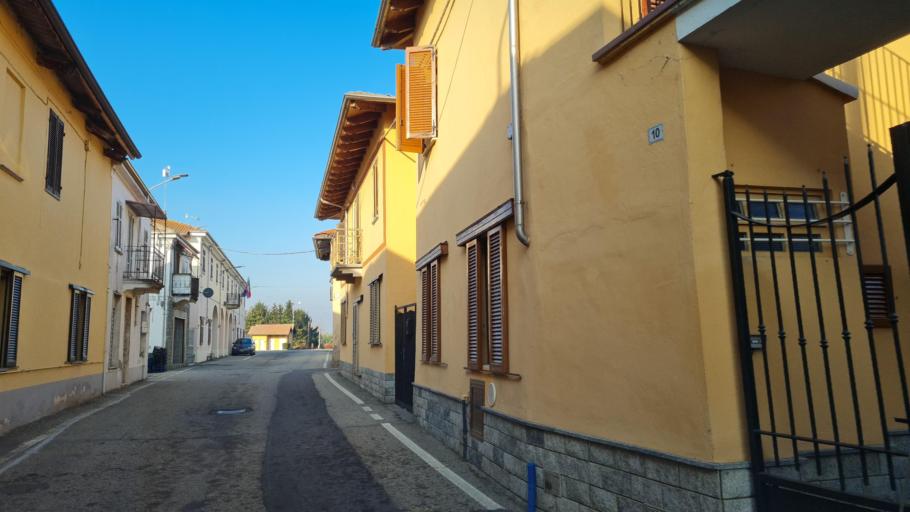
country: IT
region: Piedmont
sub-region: Provincia di Vercelli
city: Villarboit
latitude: 45.4364
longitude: 8.3377
